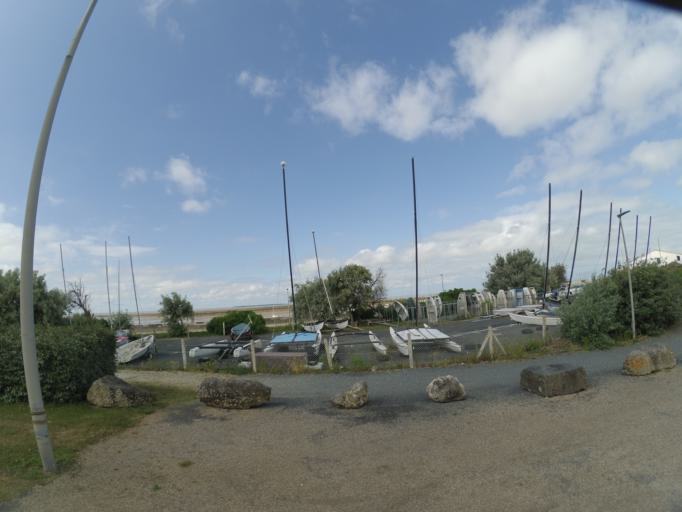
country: FR
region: Poitou-Charentes
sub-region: Departement de la Charente-Maritime
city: Chatelaillon-Plage
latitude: 46.0615
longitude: -1.0913
